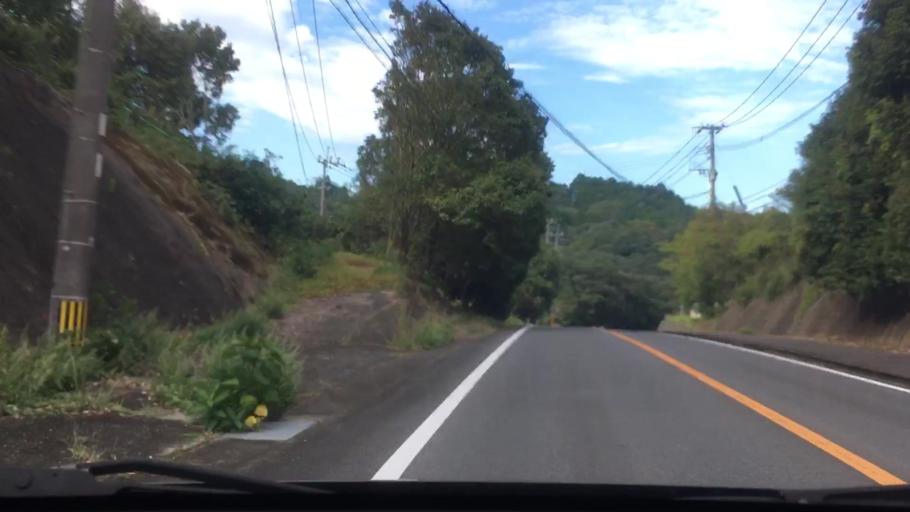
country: JP
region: Nagasaki
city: Togitsu
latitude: 32.9479
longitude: 129.6629
